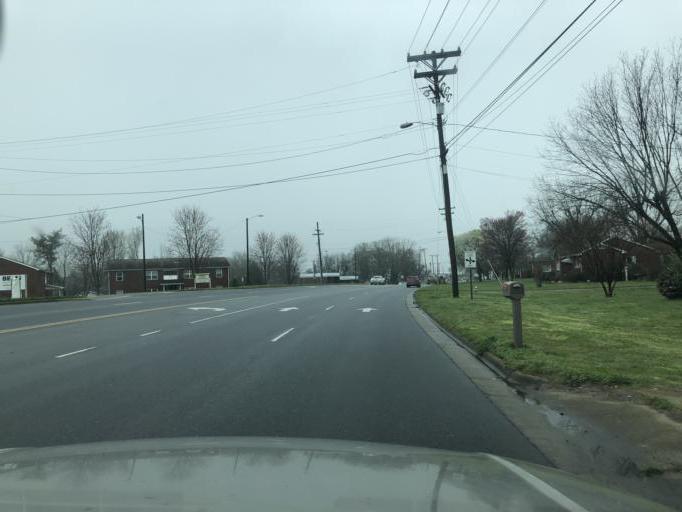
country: US
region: North Carolina
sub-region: Cleveland County
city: Shelby
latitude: 35.2778
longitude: -81.4945
